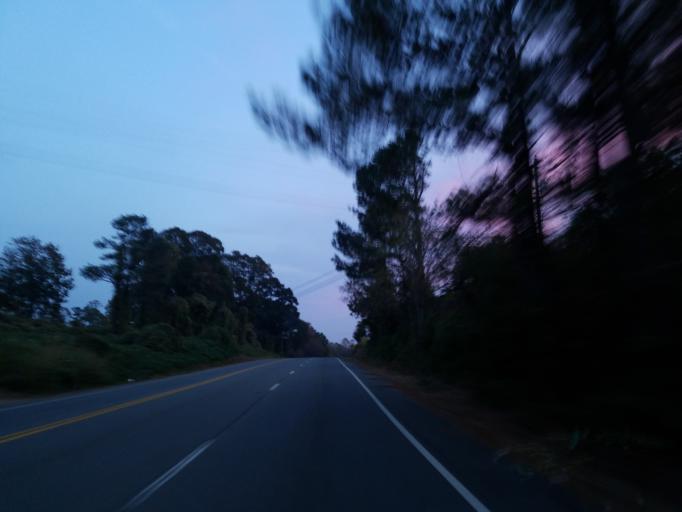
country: US
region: Georgia
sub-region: Pickens County
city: Jasper
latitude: 34.4910
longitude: -84.4620
